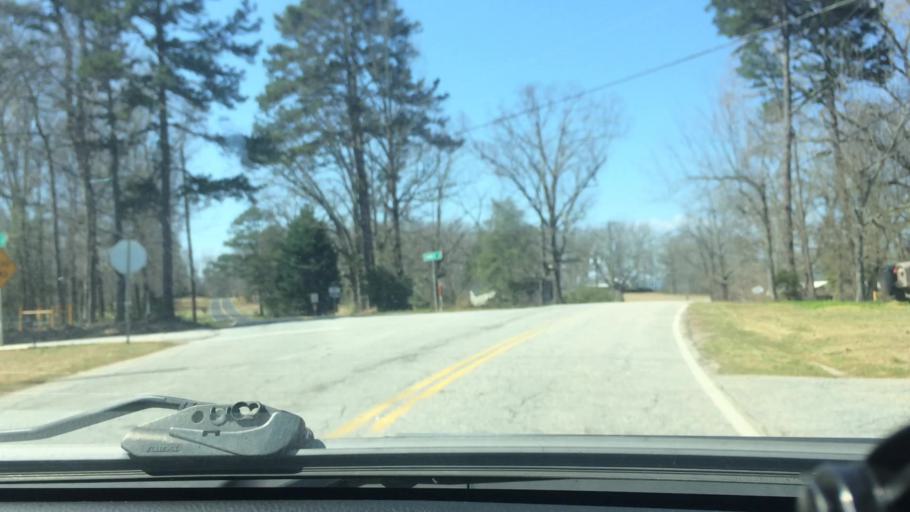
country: US
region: South Carolina
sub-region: Anderson County
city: Powdersville
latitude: 34.7905
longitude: -82.5031
